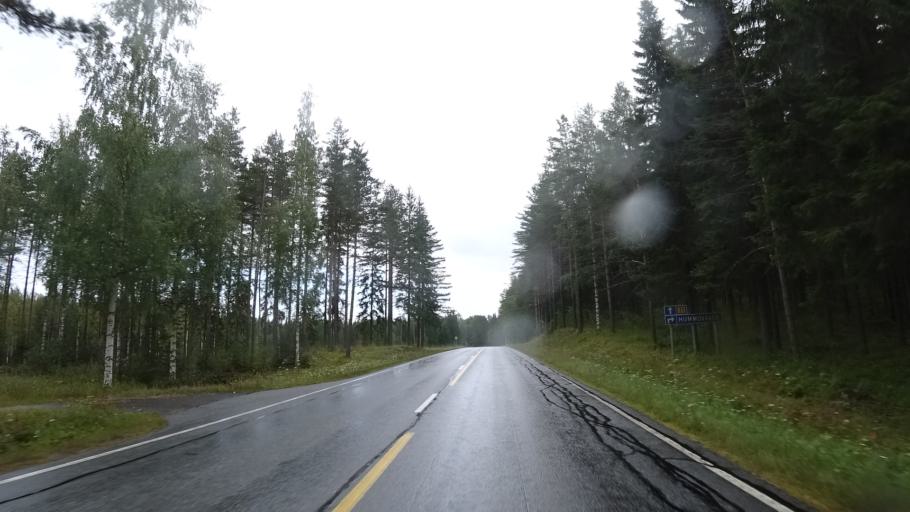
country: FI
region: North Karelia
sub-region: Keski-Karjala
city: Raeaekkylae
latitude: 62.0760
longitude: 29.6439
